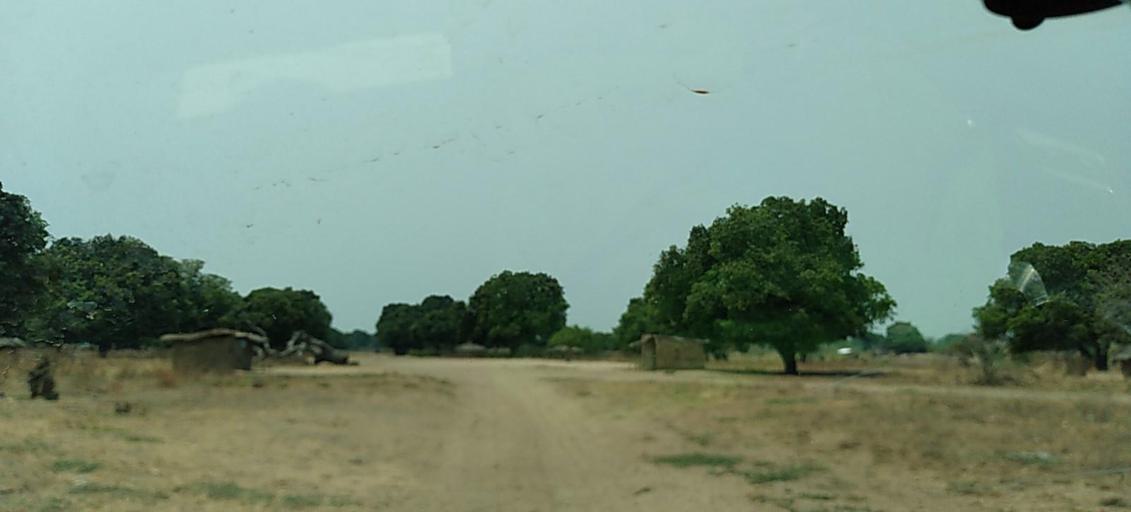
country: ZM
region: Western
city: Lukulu
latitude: -14.1581
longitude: 23.3098
